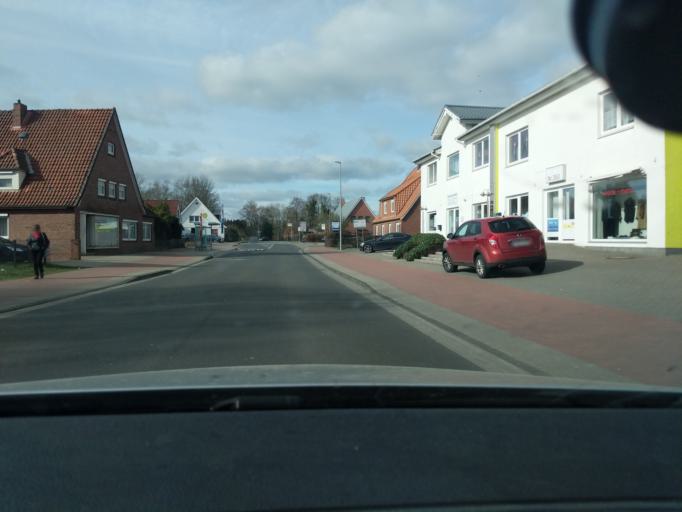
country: DE
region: Lower Saxony
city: Stade
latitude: 53.6552
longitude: 9.4793
